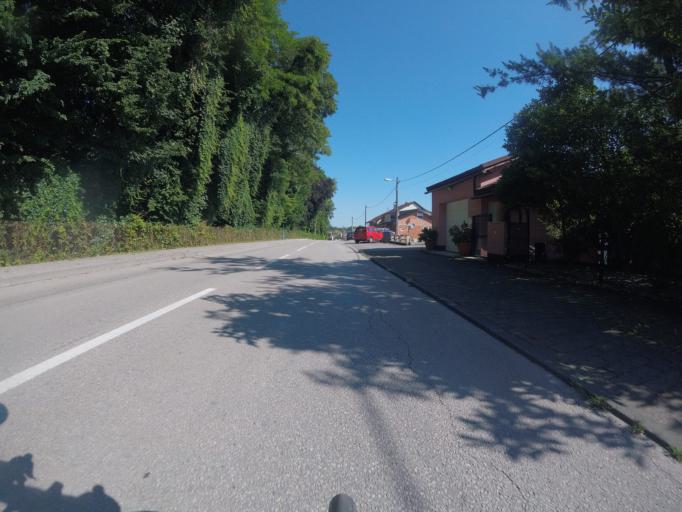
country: HR
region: Zagrebacka
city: Bregana
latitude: 45.8222
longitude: 15.6986
